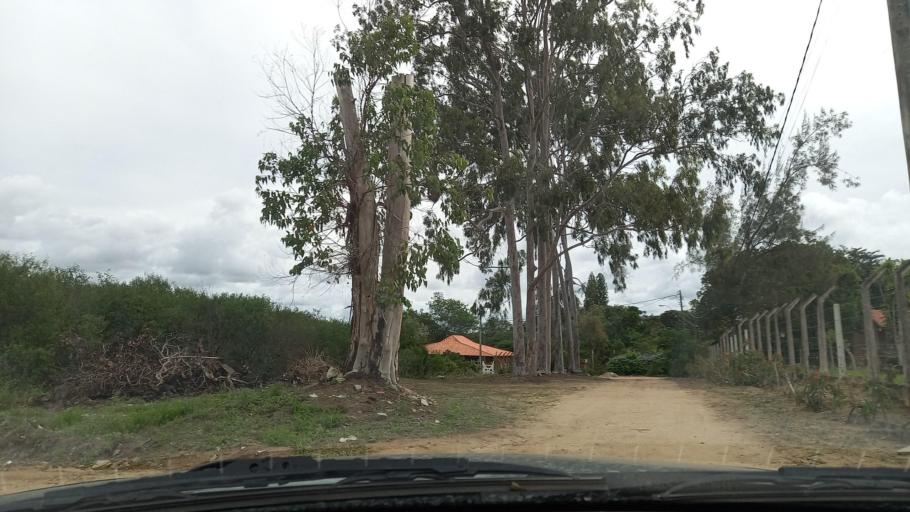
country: BR
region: Pernambuco
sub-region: Gravata
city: Gravata
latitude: -8.1917
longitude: -35.6000
